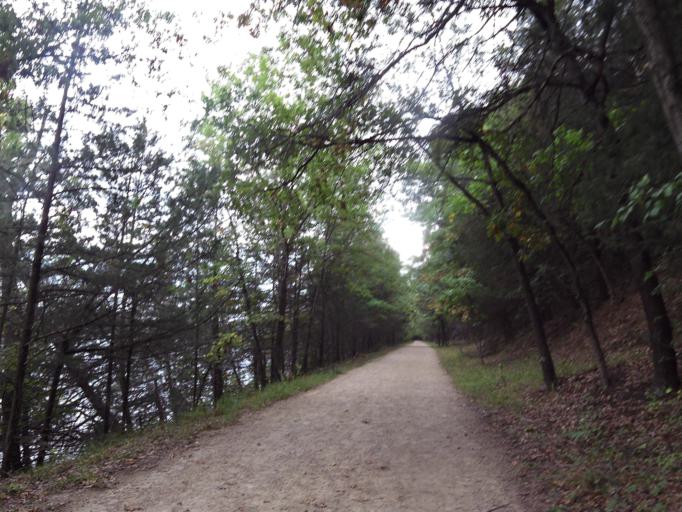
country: US
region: Minnesota
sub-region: Washington County
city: Afton
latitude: 44.8665
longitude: -92.7719
